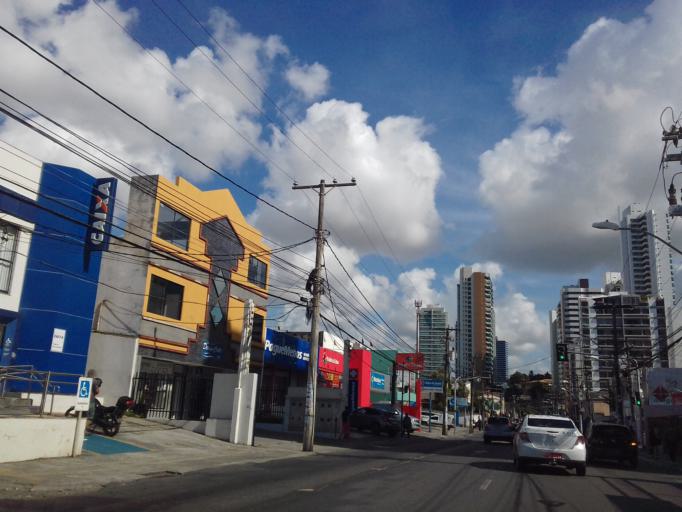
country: BR
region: Bahia
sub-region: Salvador
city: Salvador
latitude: -12.9928
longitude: -38.4547
